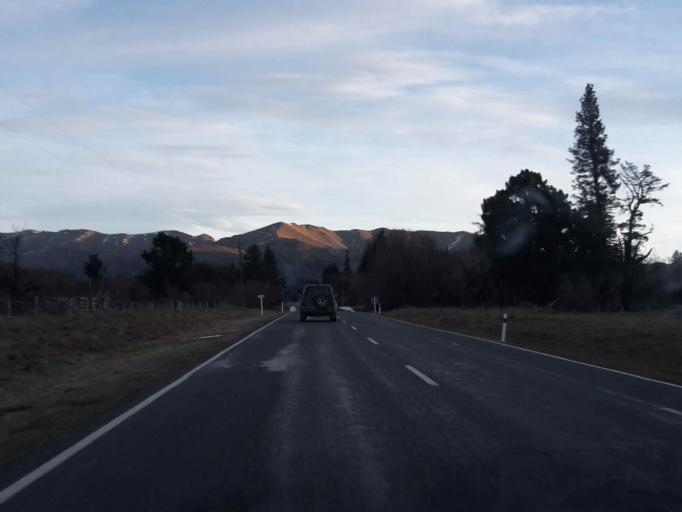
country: NZ
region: Canterbury
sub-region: Timaru District
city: Pleasant Point
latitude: -44.0818
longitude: 170.6615
